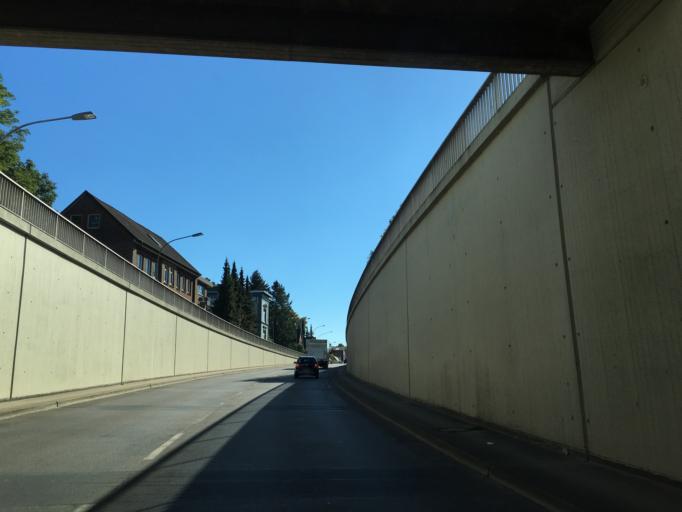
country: DE
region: Lower Saxony
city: Winsen
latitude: 53.3542
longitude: 10.2060
